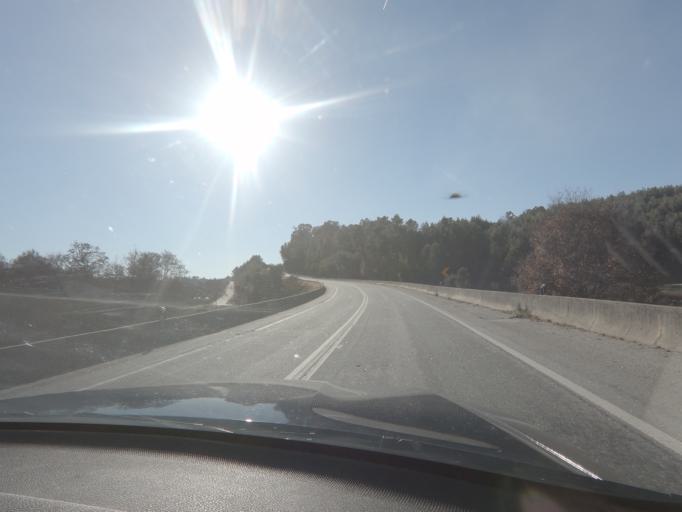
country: PT
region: Viseu
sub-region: Viseu
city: Abraveses
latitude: 40.6648
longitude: -8.0029
